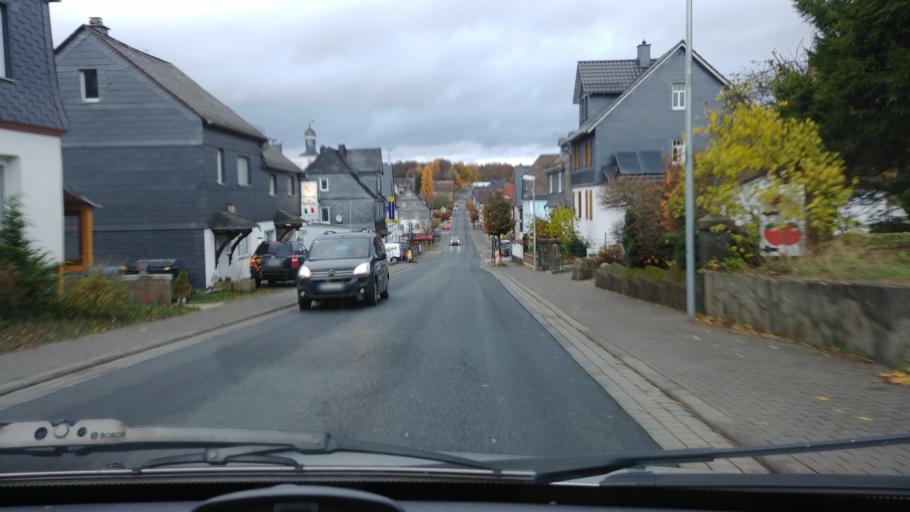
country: DE
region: Hesse
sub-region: Regierungsbezirk Giessen
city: Driedorf
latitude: 50.6319
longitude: 8.1880
